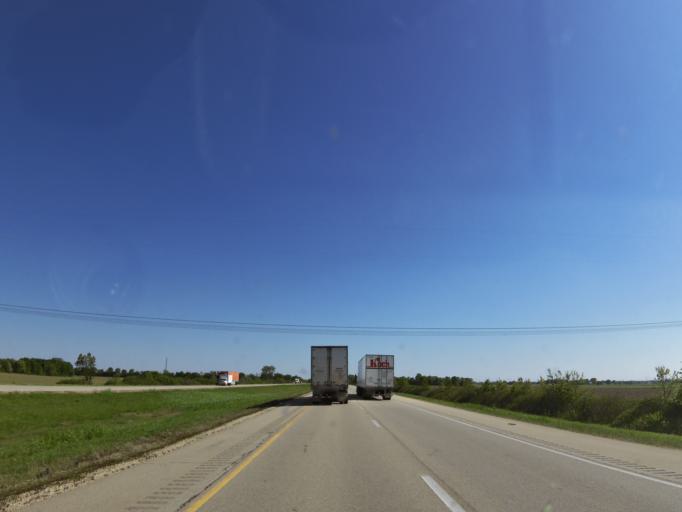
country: US
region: Illinois
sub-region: Ogle County
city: Rochelle
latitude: 41.8023
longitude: -89.0097
